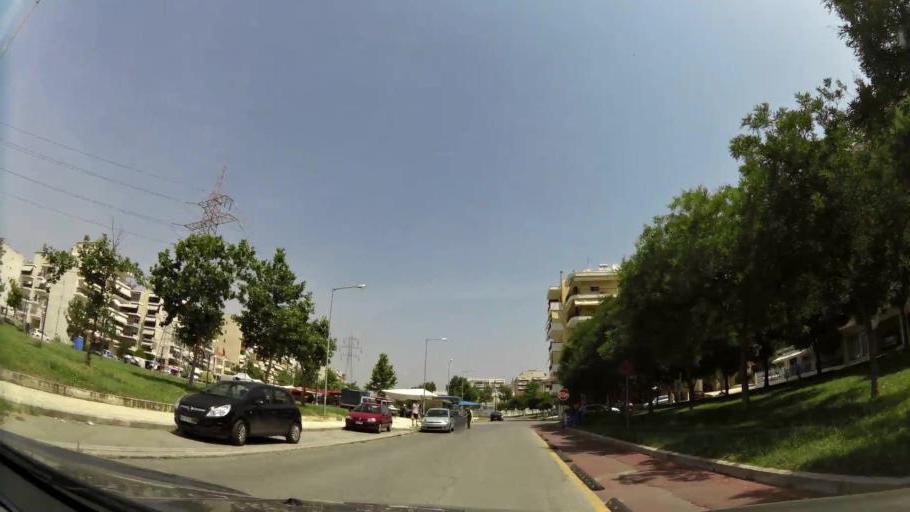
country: GR
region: Central Macedonia
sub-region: Nomos Thessalonikis
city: Evosmos
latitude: 40.6737
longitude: 22.9030
